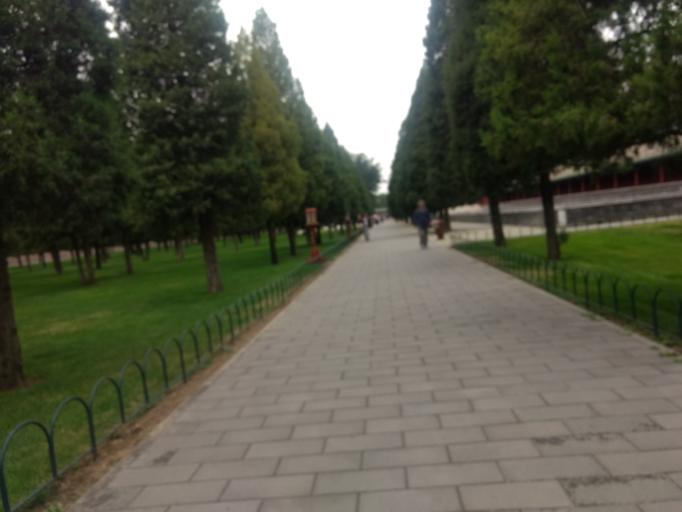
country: CN
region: Beijing
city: Longtan
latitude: 39.8774
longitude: 116.4022
